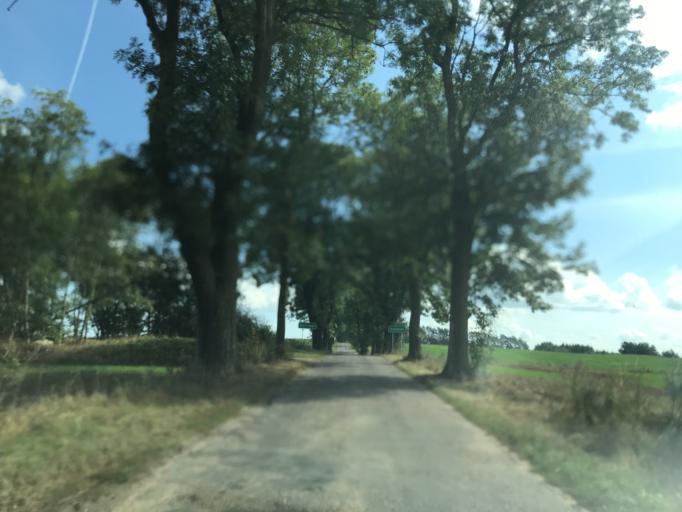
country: PL
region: Kujawsko-Pomorskie
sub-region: Powiat brodnicki
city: Brzozie
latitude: 53.3567
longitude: 19.6217
